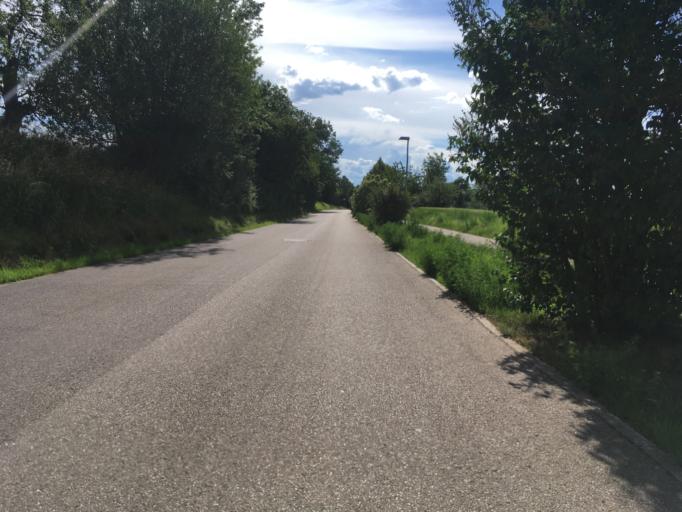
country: DE
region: Baden-Wuerttemberg
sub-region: Regierungsbezirk Stuttgart
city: Vaihingen an der Enz
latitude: 48.9401
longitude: 8.9695
